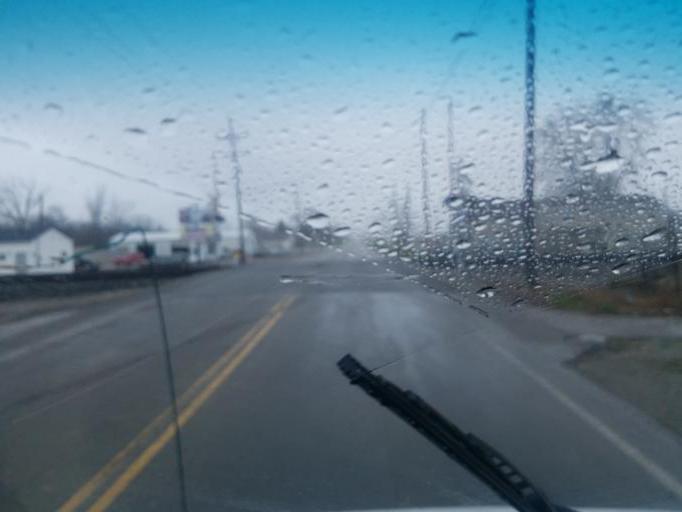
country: US
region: Ohio
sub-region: Hancock County
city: Findlay
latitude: 41.1108
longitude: -83.6498
